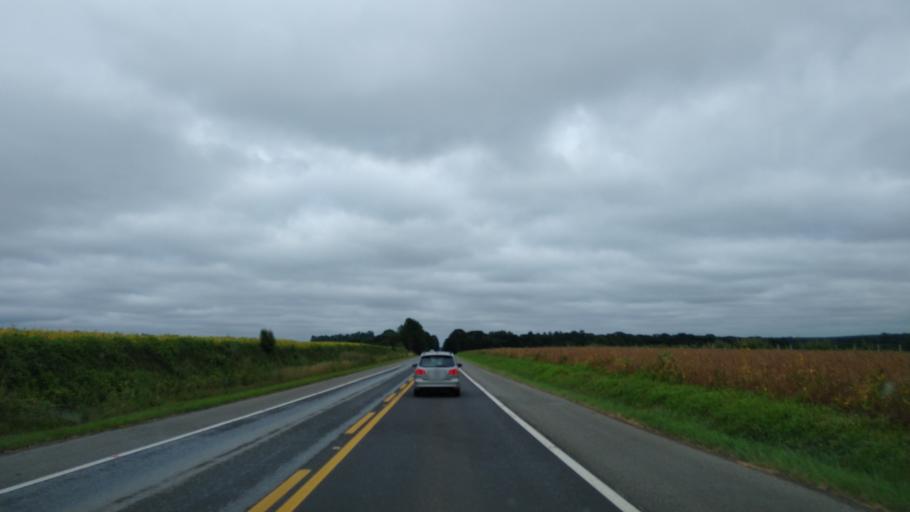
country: BR
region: Santa Catarina
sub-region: Tres Barras
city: Tres Barras
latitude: -26.1664
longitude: -50.1092
